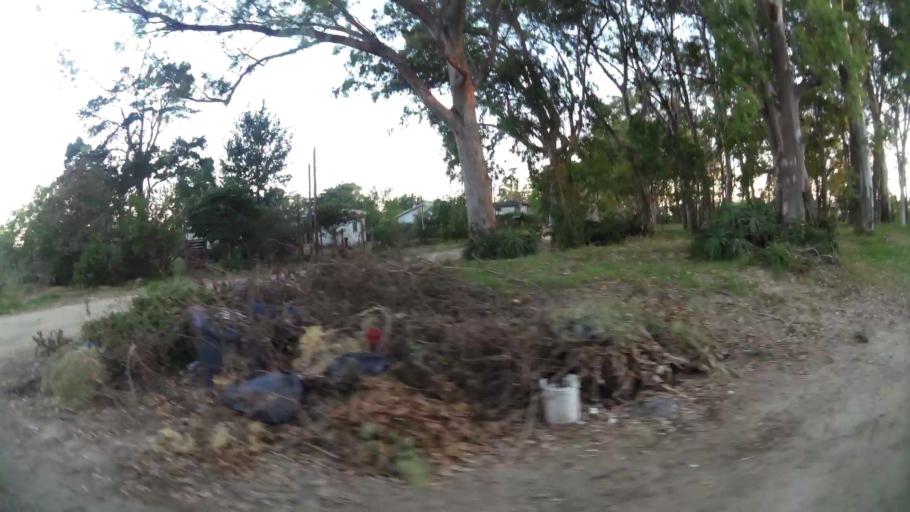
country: UY
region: Canelones
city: Barra de Carrasco
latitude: -34.8288
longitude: -55.9605
